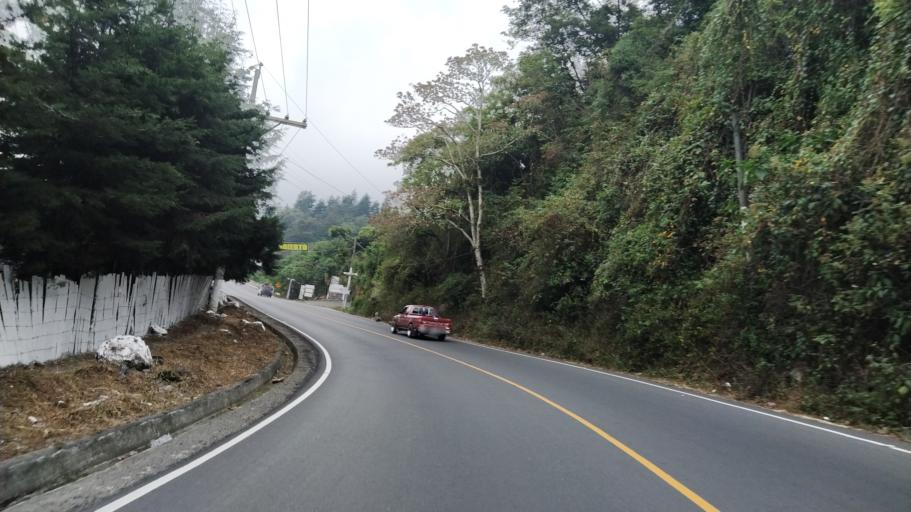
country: GT
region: Quetzaltenango
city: Zunil
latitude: 14.7294
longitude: -91.5248
